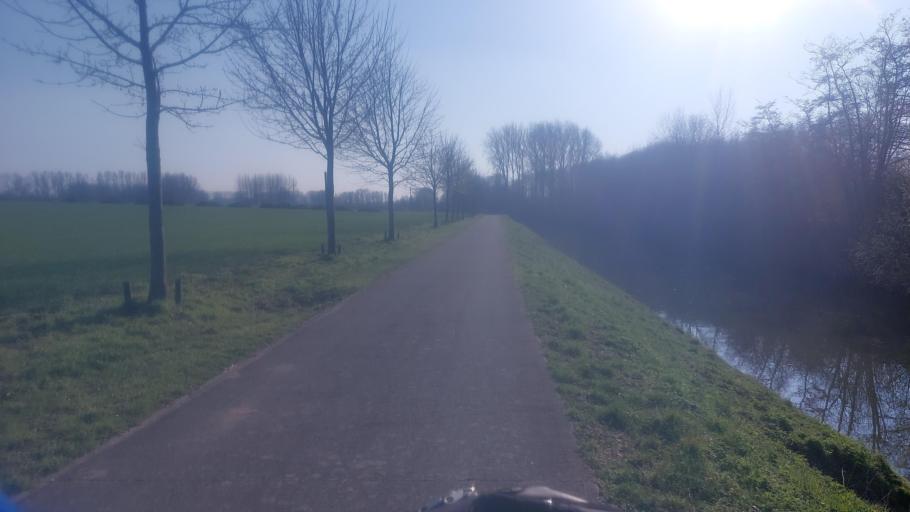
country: BE
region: Wallonia
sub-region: Province du Hainaut
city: Ath
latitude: 50.6620
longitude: 3.7986
